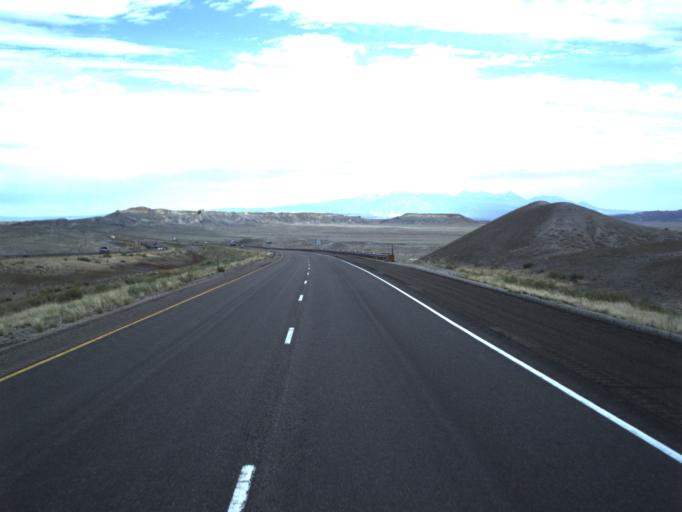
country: US
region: Utah
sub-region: Grand County
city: Moab
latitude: 38.9589
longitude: -109.7118
